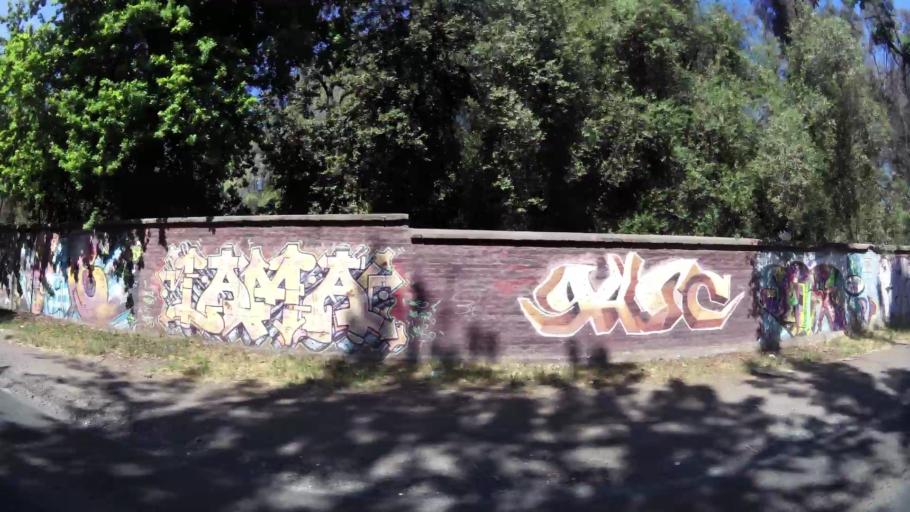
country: CL
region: Santiago Metropolitan
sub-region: Provincia de Santiago
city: Villa Presidente Frei, Nunoa, Santiago, Chile
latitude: -33.4943
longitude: -70.5701
